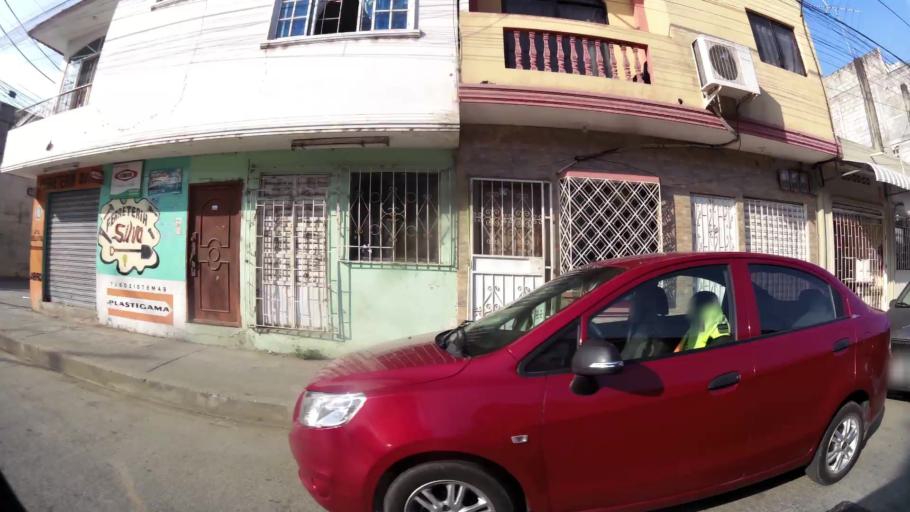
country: EC
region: Guayas
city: Eloy Alfaro
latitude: -2.1798
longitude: -79.8549
